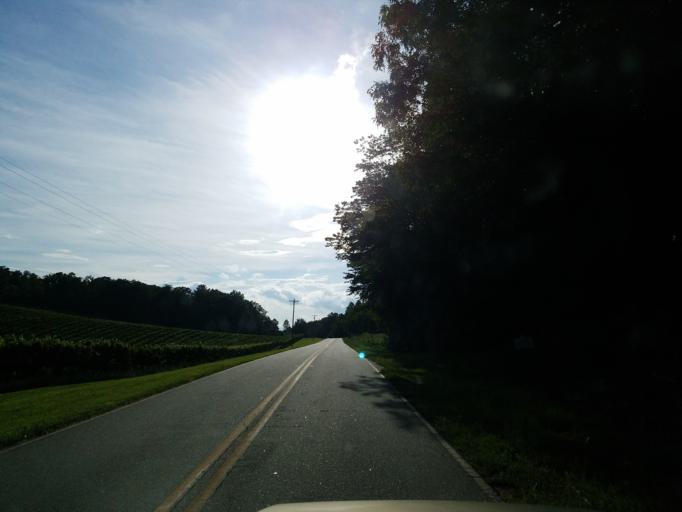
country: US
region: Georgia
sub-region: White County
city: Cleveland
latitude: 34.6153
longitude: -83.8715
